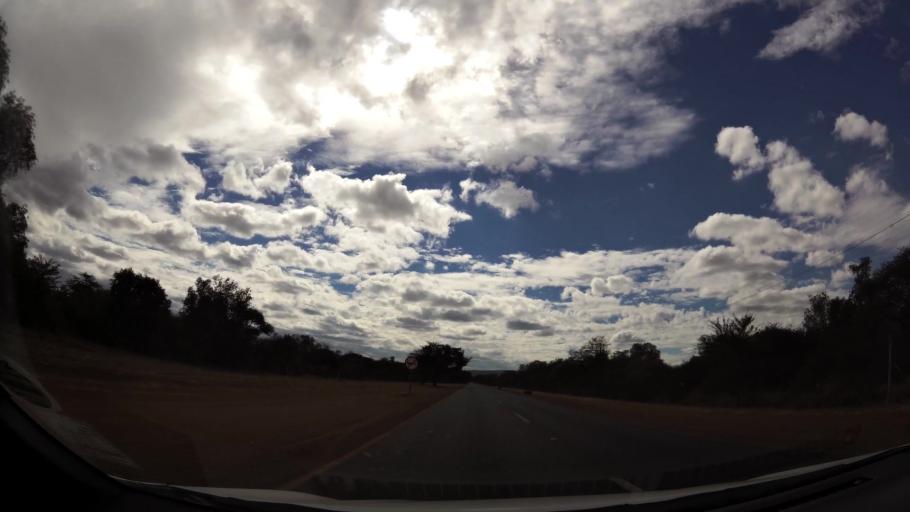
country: ZA
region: Limpopo
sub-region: Waterberg District Municipality
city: Warmbaths
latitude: -24.8956
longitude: 28.2817
